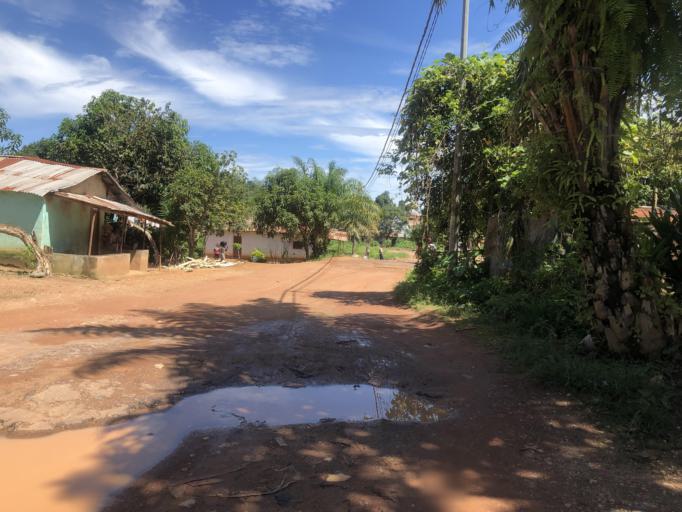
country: SL
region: Eastern Province
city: Koidu
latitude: 8.6449
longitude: -10.9547
